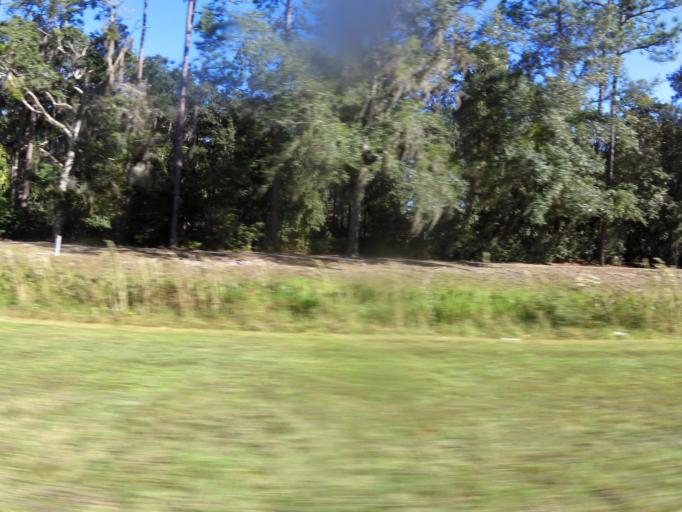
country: US
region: Florida
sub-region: Alachua County
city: Alachua
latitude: 29.7110
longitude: -82.3884
